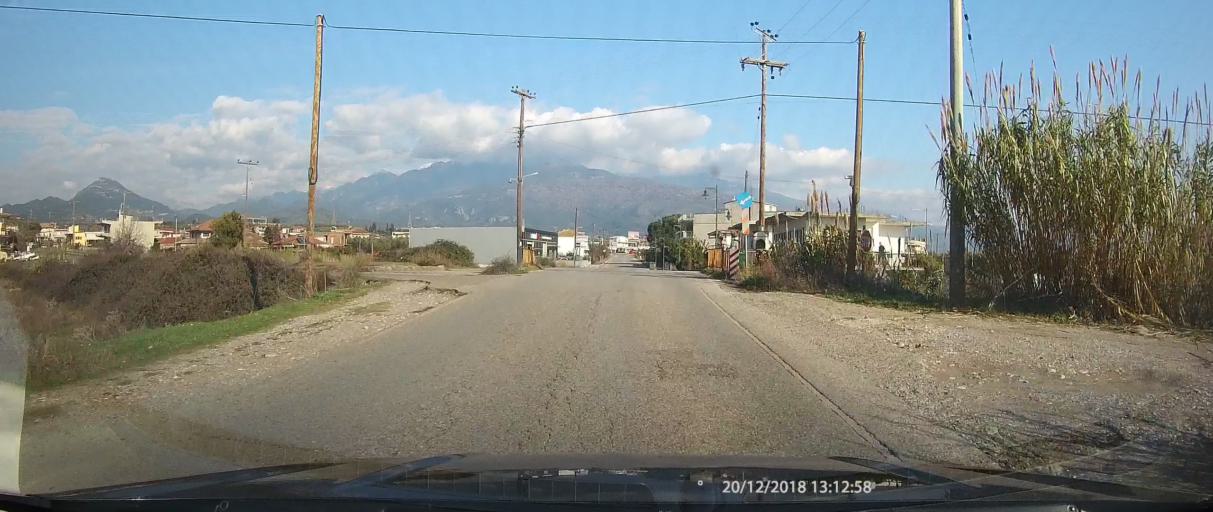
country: GR
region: West Greece
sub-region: Nomos Aitolias kai Akarnanias
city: Kainouryion
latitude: 38.6009
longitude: 21.4751
